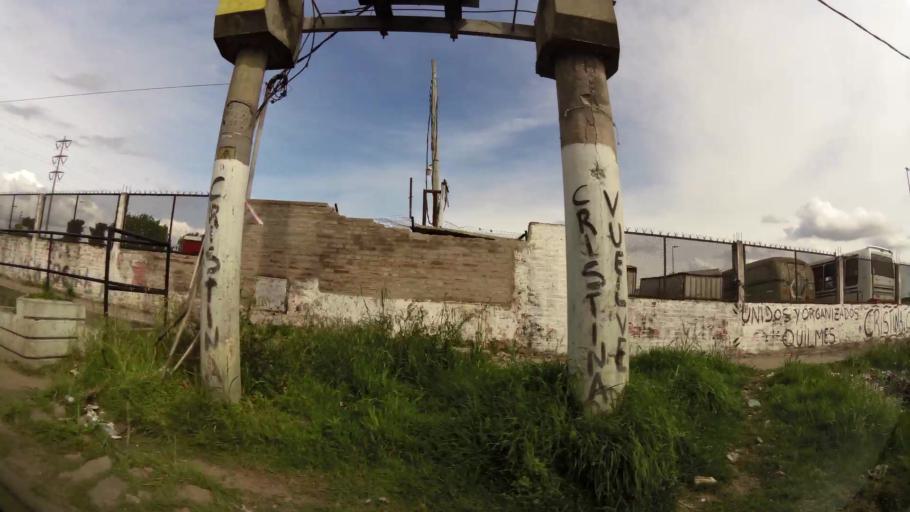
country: AR
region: Buenos Aires
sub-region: Partido de Quilmes
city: Quilmes
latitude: -34.7652
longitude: -58.2511
